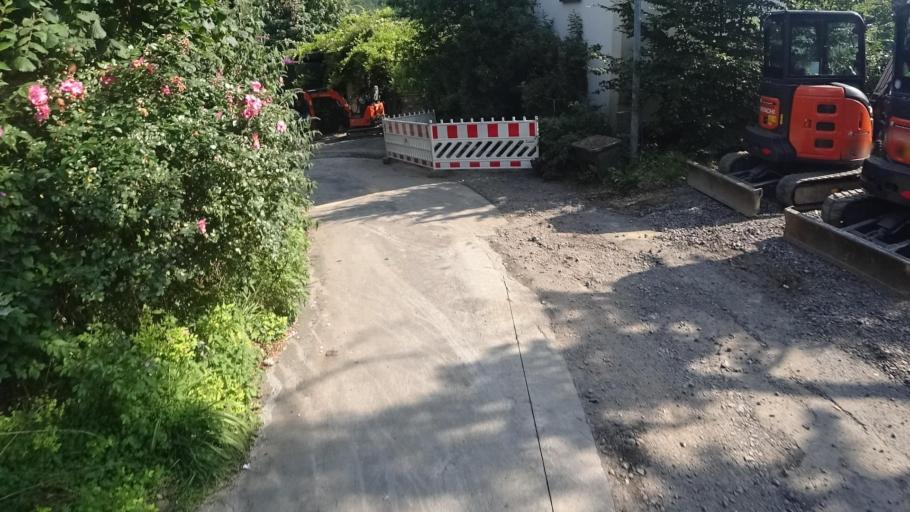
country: DE
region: Rheinland-Pfalz
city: Sankt Katharinen
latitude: 50.5584
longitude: 7.3577
